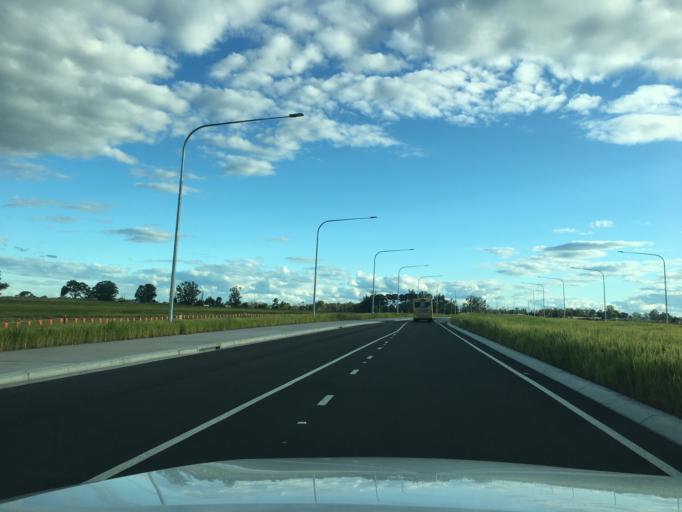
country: AU
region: New South Wales
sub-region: Liverpool
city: Bringelly
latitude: -33.8797
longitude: 150.7460
